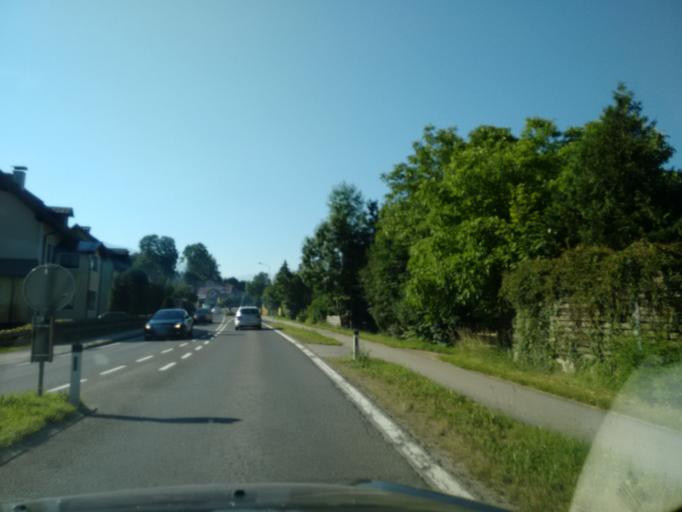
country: AT
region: Upper Austria
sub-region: Politischer Bezirk Gmunden
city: Bad Goisern
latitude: 47.6540
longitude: 13.6103
